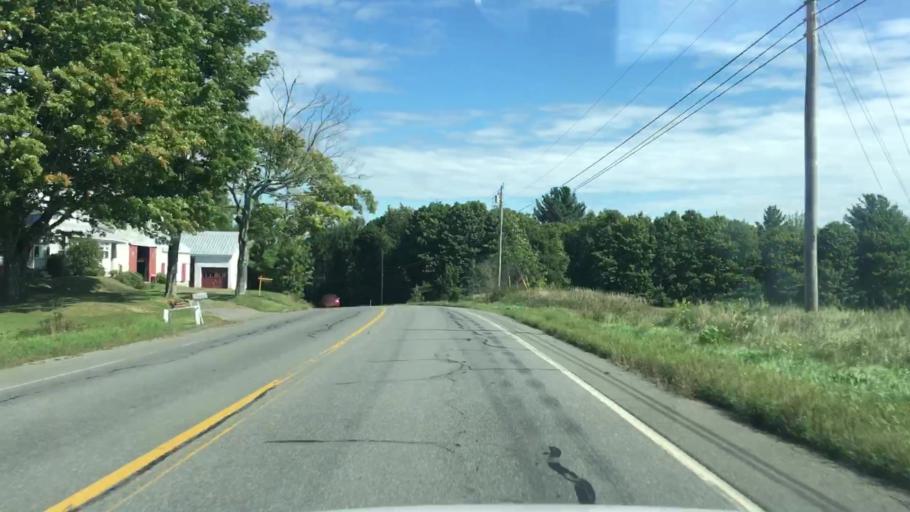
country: US
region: Maine
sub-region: Penobscot County
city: Dexter
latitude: 45.0753
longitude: -69.2327
